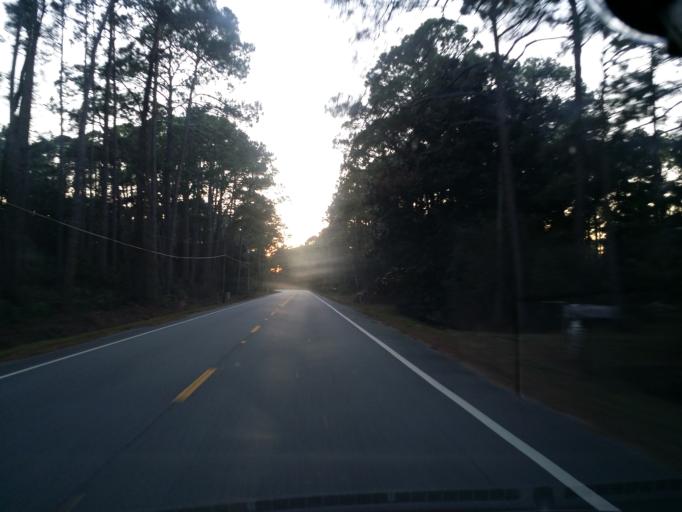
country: US
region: Florida
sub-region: Franklin County
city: Carrabelle
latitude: 29.8078
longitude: -84.7304
